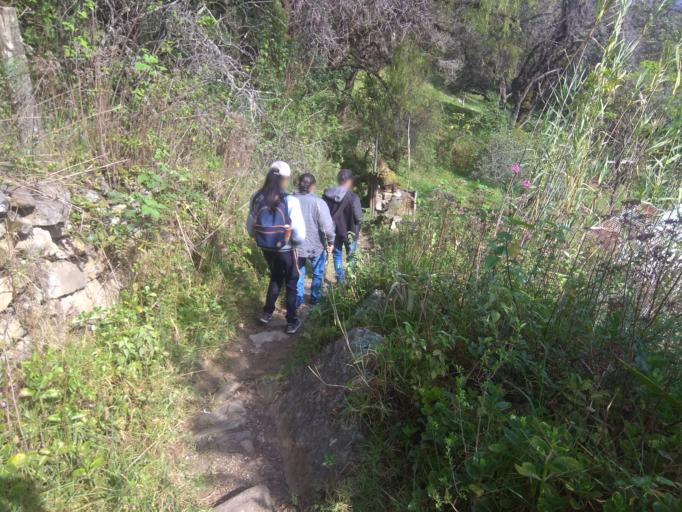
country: CO
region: Boyaca
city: Socha Viejo
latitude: 5.9790
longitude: -72.7053
